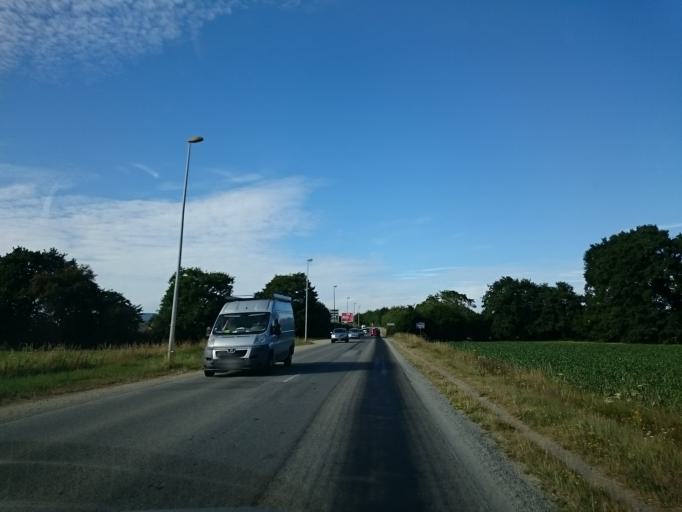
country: FR
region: Brittany
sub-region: Departement d'Ille-et-Vilaine
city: Chantepie
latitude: 48.0814
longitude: -1.6299
